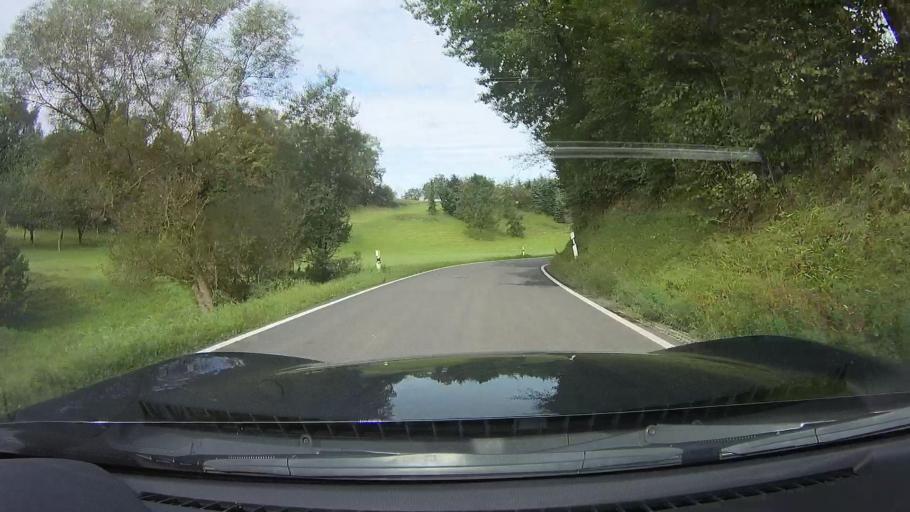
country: DE
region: Baden-Wuerttemberg
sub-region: Regierungsbezirk Stuttgart
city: Lowenstein
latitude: 49.0506
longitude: 9.4053
